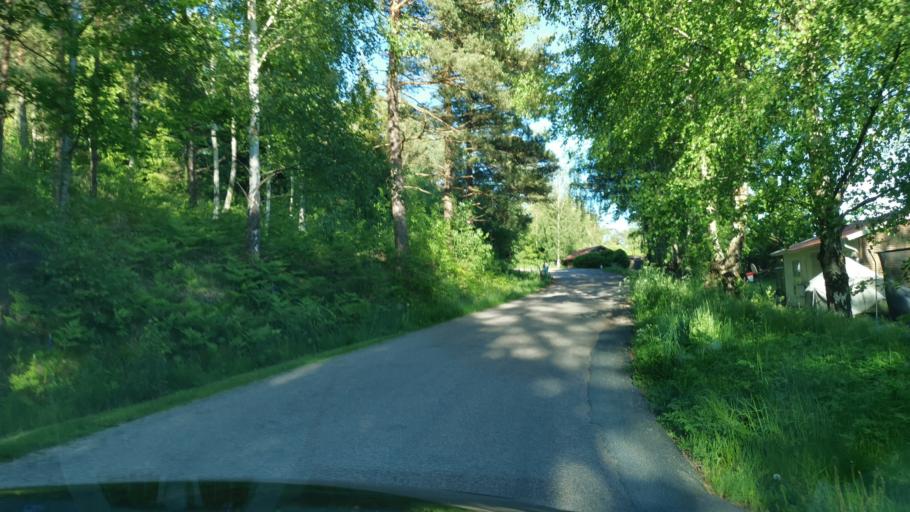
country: SE
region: Vaestra Goetaland
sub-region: Orust
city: Henan
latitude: 58.2660
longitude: 11.6269
